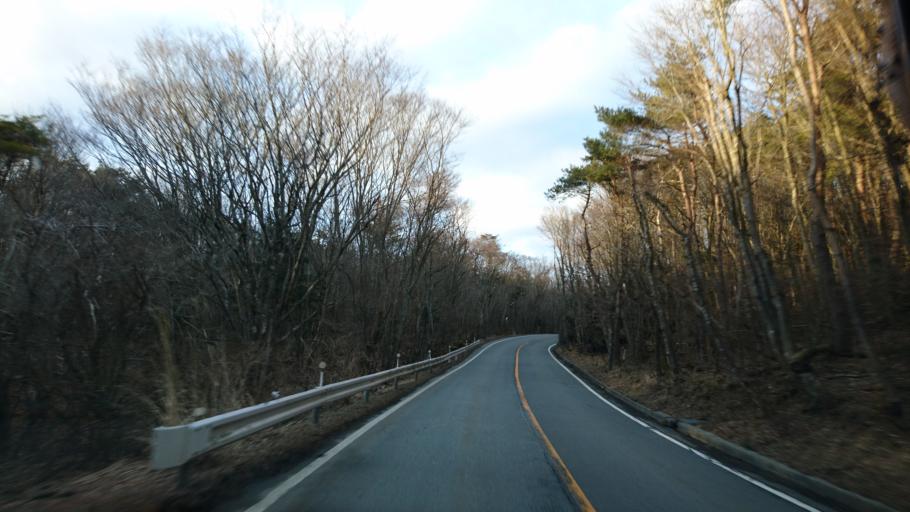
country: JP
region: Yamanashi
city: Fujikawaguchiko
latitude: 35.4457
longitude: 138.6404
